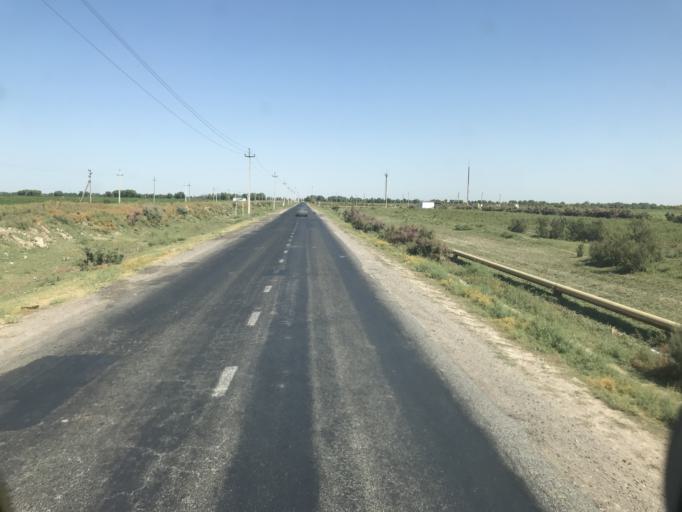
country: KZ
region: Ongtustik Qazaqstan
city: Ilyich
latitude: 40.9028
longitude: 68.4882
